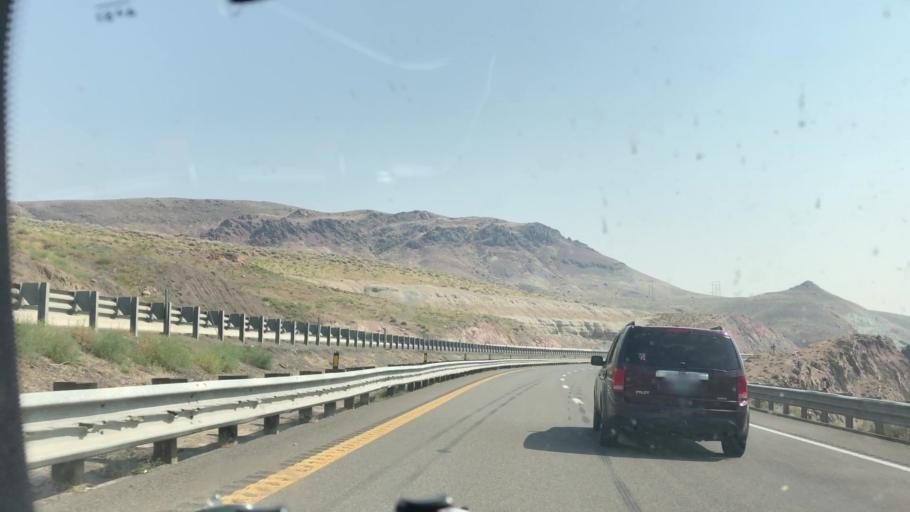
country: US
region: Nevada
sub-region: Lyon County
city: Fernley
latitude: 39.5949
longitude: -119.3656
